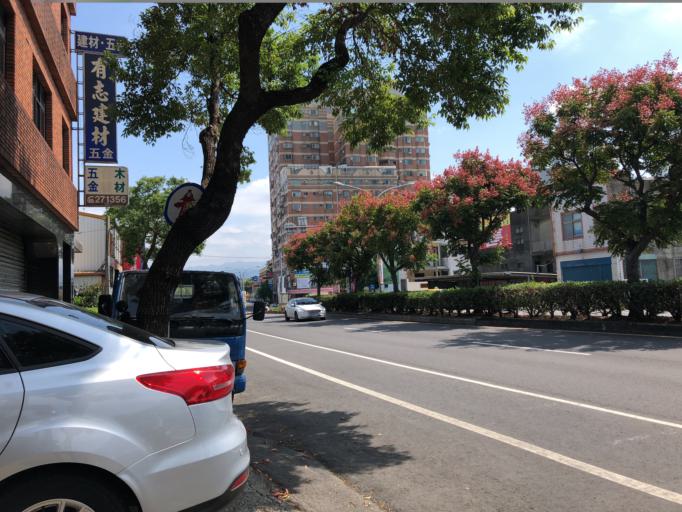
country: TW
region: Taiwan
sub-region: Miaoli
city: Miaoli
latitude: 24.5757
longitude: 120.8237
